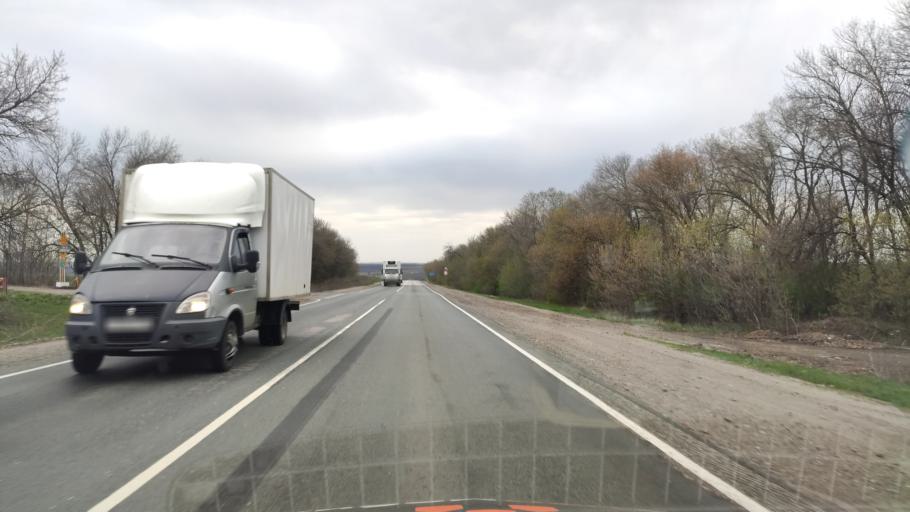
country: RU
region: Voronezj
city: Nizhnedevitsk
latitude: 51.5807
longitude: 38.4925
